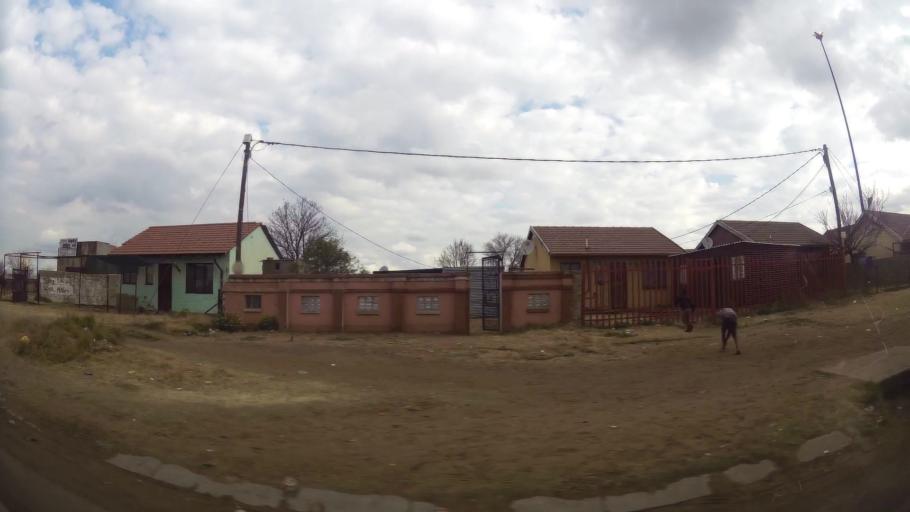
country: ZA
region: Orange Free State
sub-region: Fezile Dabi District Municipality
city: Sasolburg
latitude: -26.8513
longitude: 27.8617
